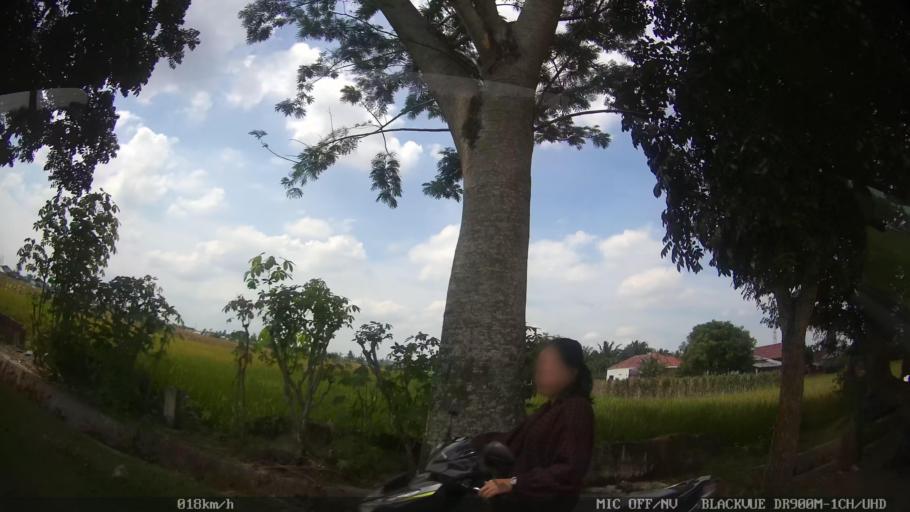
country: ID
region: North Sumatra
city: Binjai
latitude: 3.6209
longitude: 98.5153
